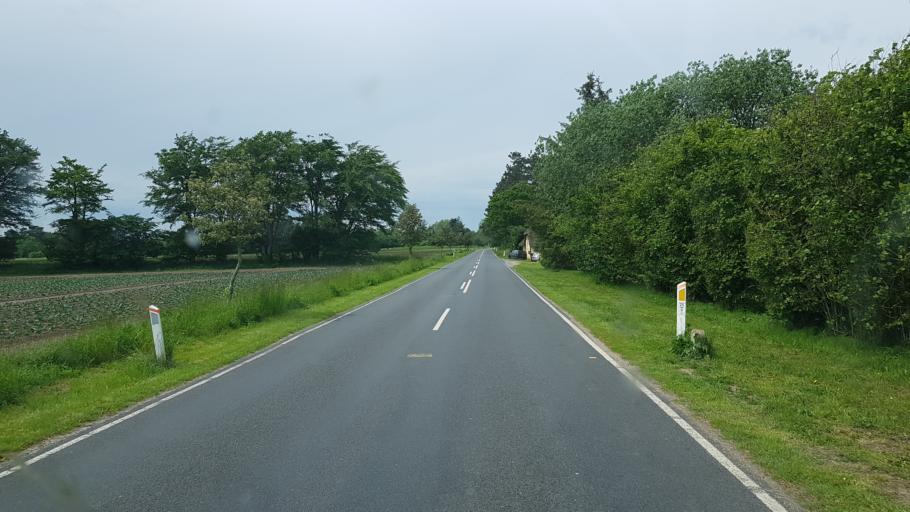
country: DK
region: South Denmark
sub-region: Nordfyns Kommune
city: Sonderso
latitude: 55.5626
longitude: 10.2248
